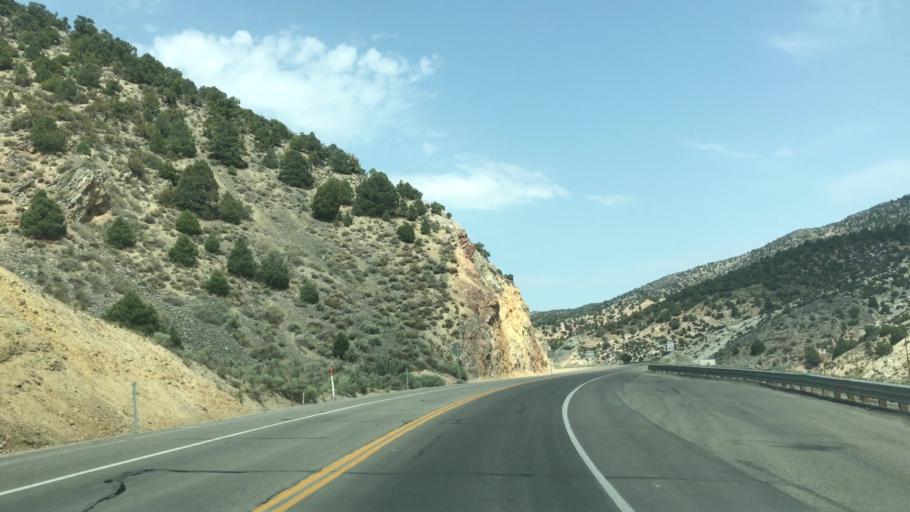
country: US
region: Nevada
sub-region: White Pine County
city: Ely
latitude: 39.2471
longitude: -114.9065
